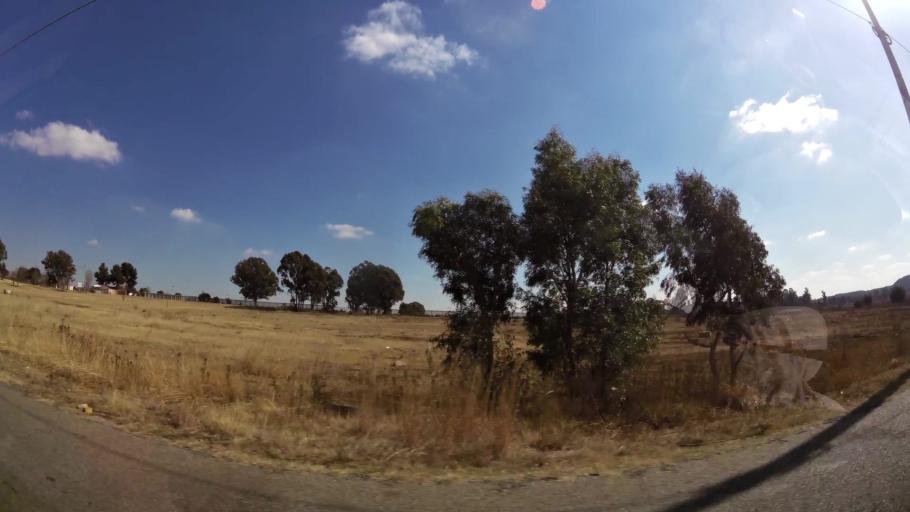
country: ZA
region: Gauteng
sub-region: West Rand District Municipality
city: Randfontein
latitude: -26.1548
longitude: 27.7624
